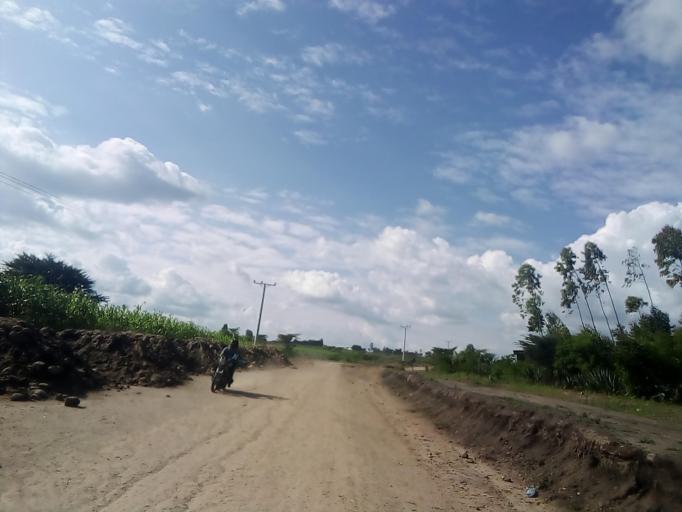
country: ET
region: Southern Nations, Nationalities, and People's Region
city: K'olito
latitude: 7.6257
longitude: 38.0639
